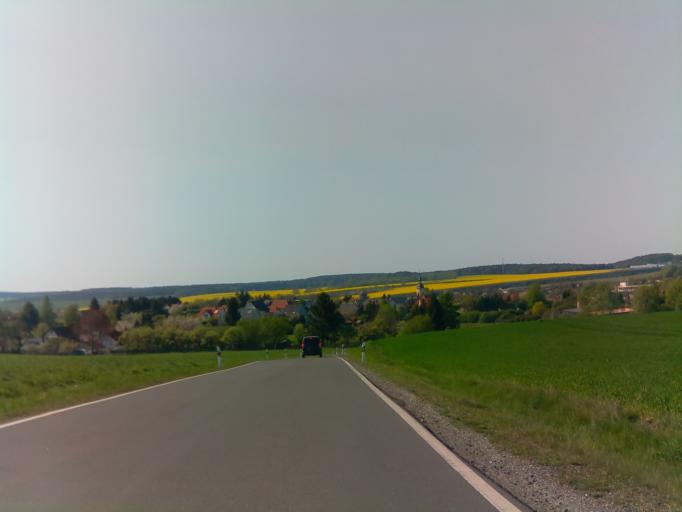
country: DE
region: Thuringia
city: Triptis
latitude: 50.7263
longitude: 11.8727
